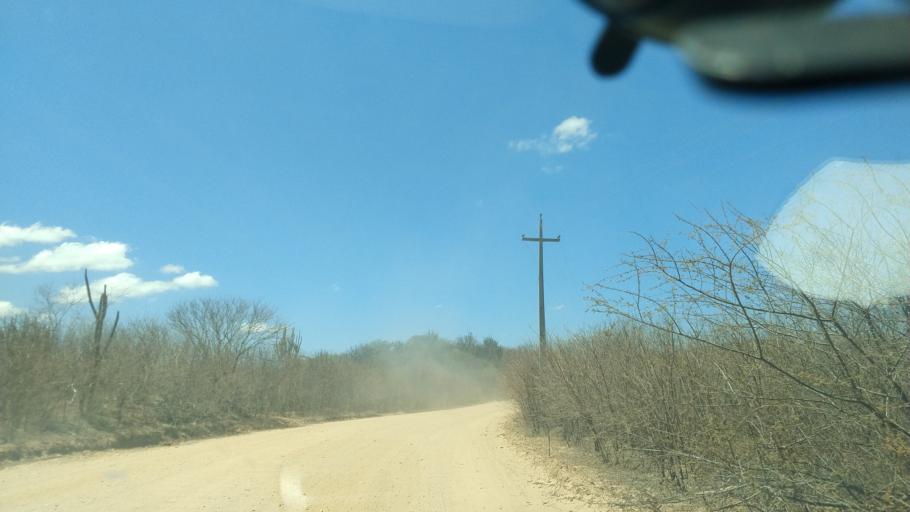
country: BR
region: Rio Grande do Norte
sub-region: Cerro Cora
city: Cerro Cora
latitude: -6.0094
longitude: -36.2842
